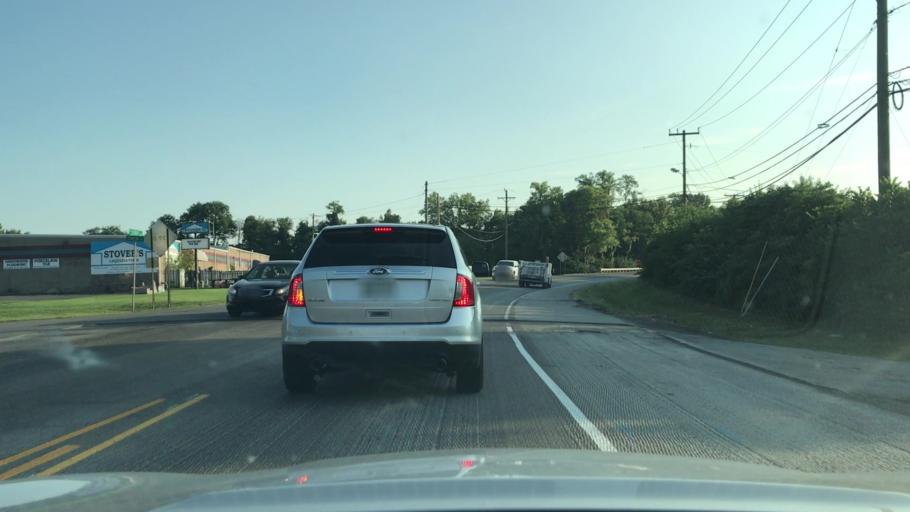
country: US
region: Tennessee
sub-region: Rutherford County
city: La Vergne
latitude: 36.0181
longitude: -86.6195
